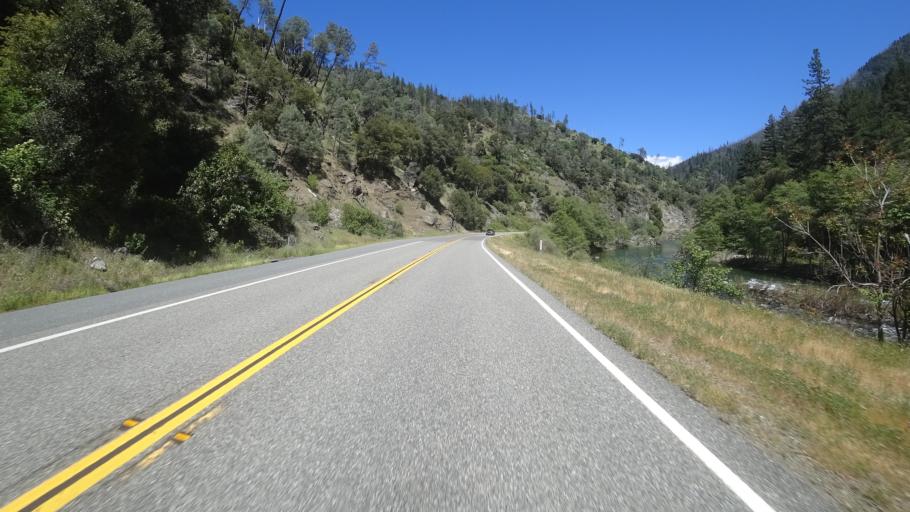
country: US
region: California
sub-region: Trinity County
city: Hayfork
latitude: 40.7508
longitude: -123.1668
